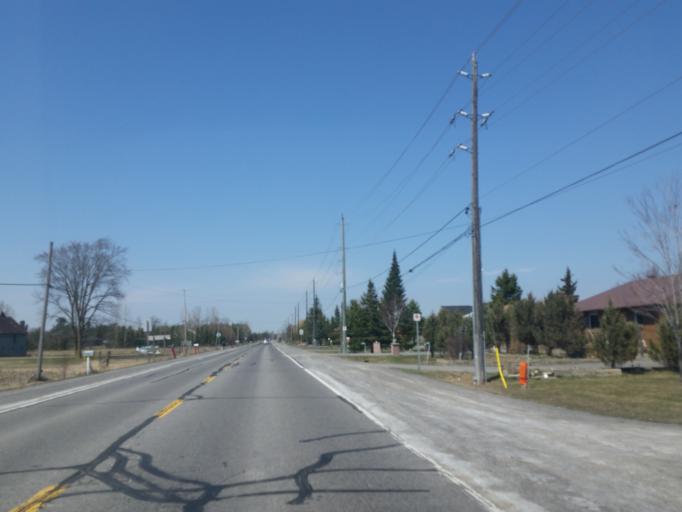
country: CA
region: Ontario
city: Bells Corners
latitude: 45.4424
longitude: -76.0484
